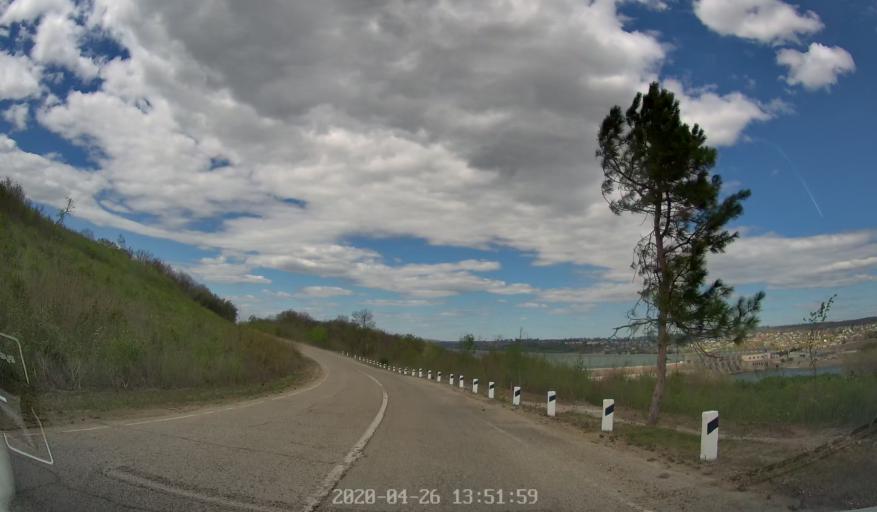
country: MD
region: Telenesti
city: Cocieri
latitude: 47.2705
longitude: 29.1209
